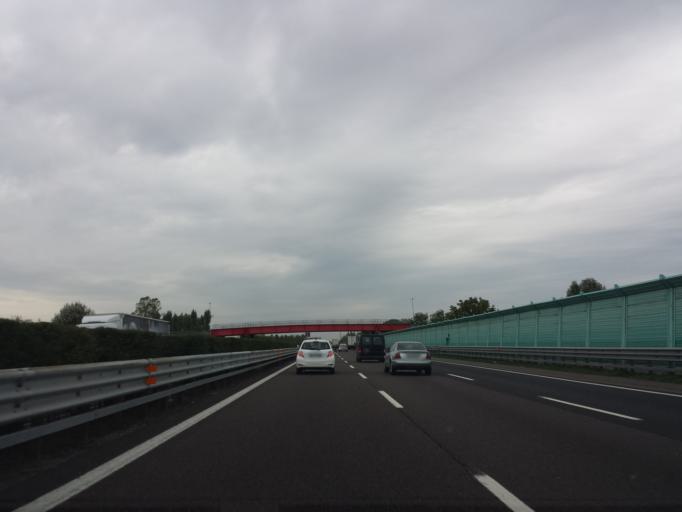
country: IT
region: Veneto
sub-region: Provincia di Venezia
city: Fornase
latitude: 45.4622
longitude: 12.1518
